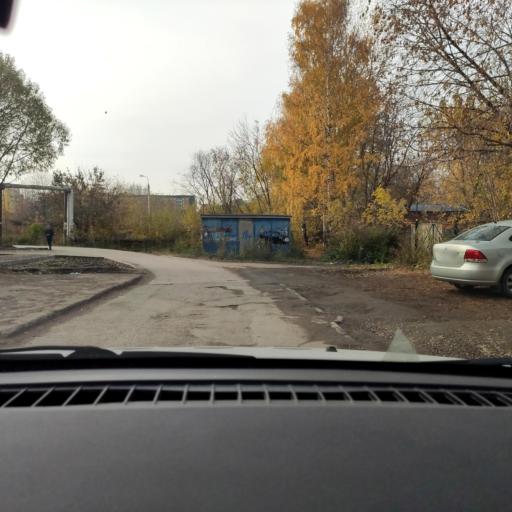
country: RU
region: Perm
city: Perm
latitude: 58.0601
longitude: 56.3544
